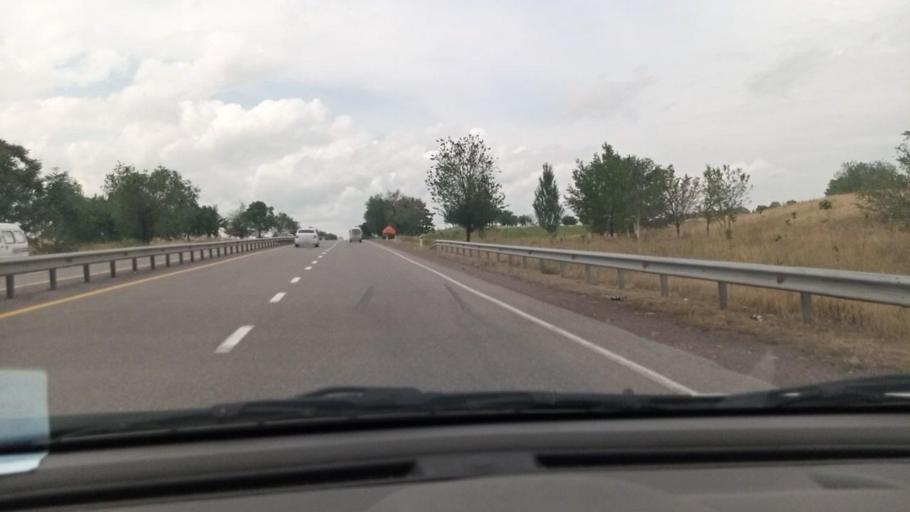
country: UZ
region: Toshkent
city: Ohangaron
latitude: 41.0055
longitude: 69.5231
